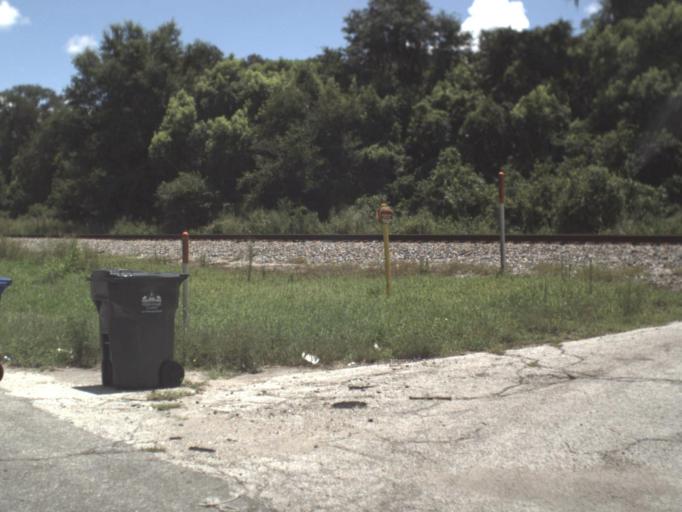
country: US
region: Florida
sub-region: Hillsborough County
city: Seffner
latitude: 27.9853
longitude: -82.2694
